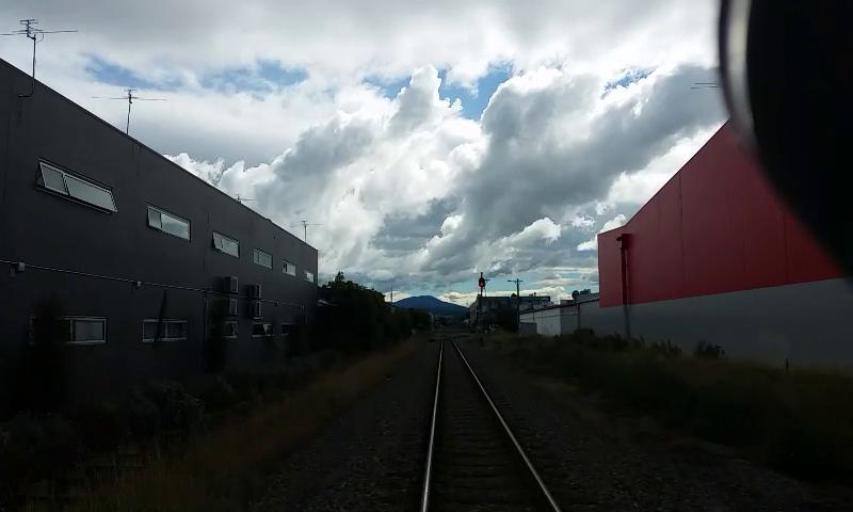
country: NZ
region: Canterbury
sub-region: Waimakariri District
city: Woodend
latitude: -43.3045
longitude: 172.5986
